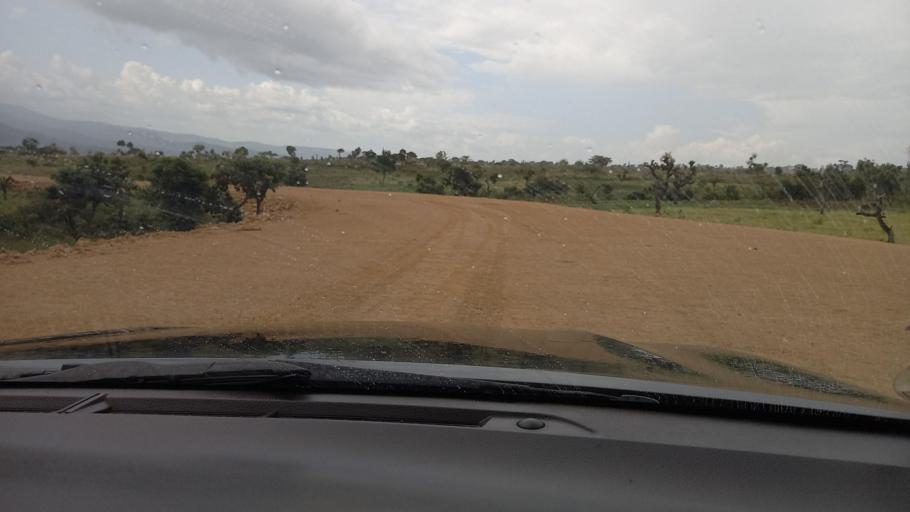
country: ET
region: Southern Nations, Nationalities, and People's Region
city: Mizan Teferi
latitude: 6.1742
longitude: 35.7067
